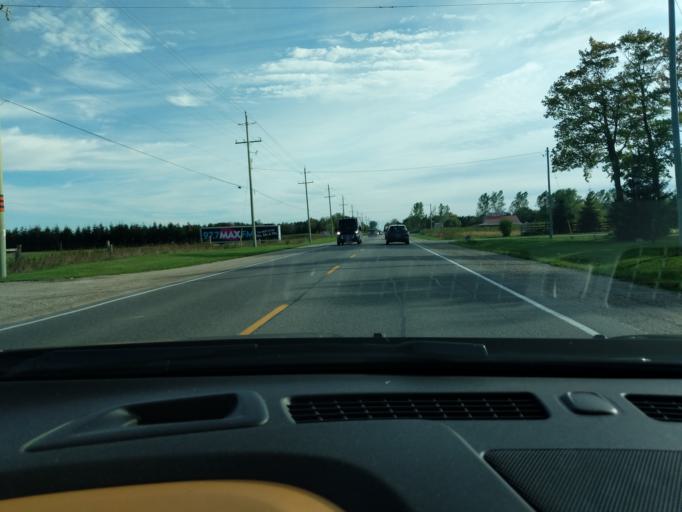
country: CA
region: Ontario
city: Wasaga Beach
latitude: 44.4419
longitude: -80.1012
